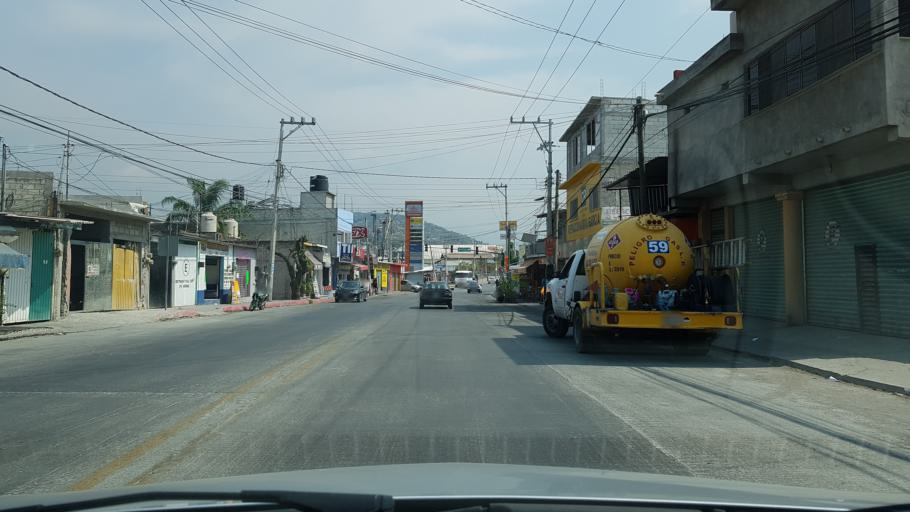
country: MX
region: Morelos
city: Emiliano Zapata
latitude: 18.8307
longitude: -99.1873
